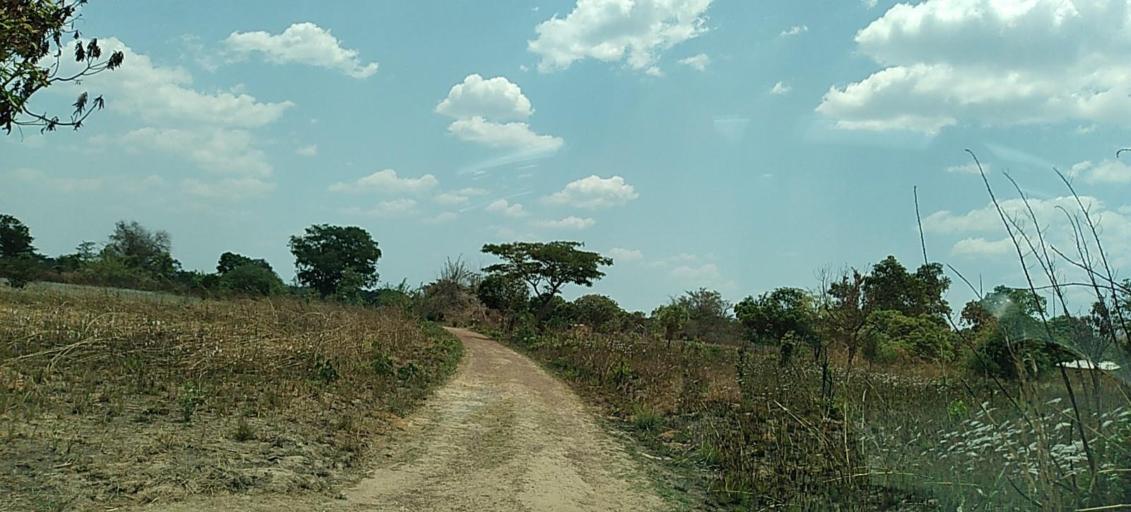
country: ZM
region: Copperbelt
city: Chililabombwe
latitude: -12.4656
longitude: 27.6683
